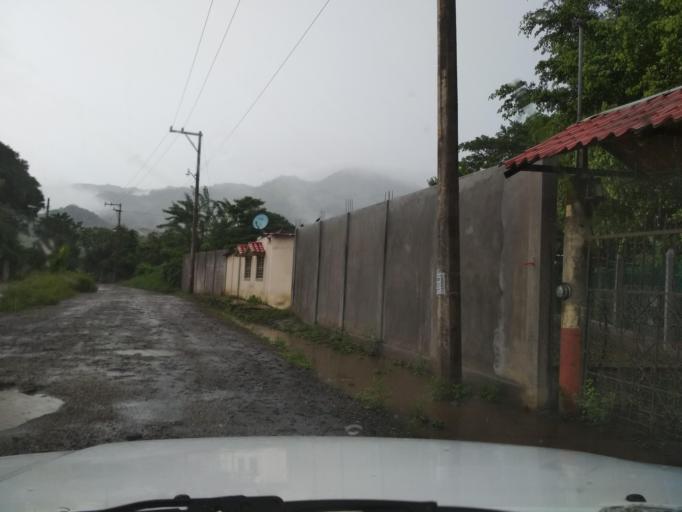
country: MX
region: Veracruz
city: Santiago Tuxtla
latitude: 18.4514
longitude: -95.3150
